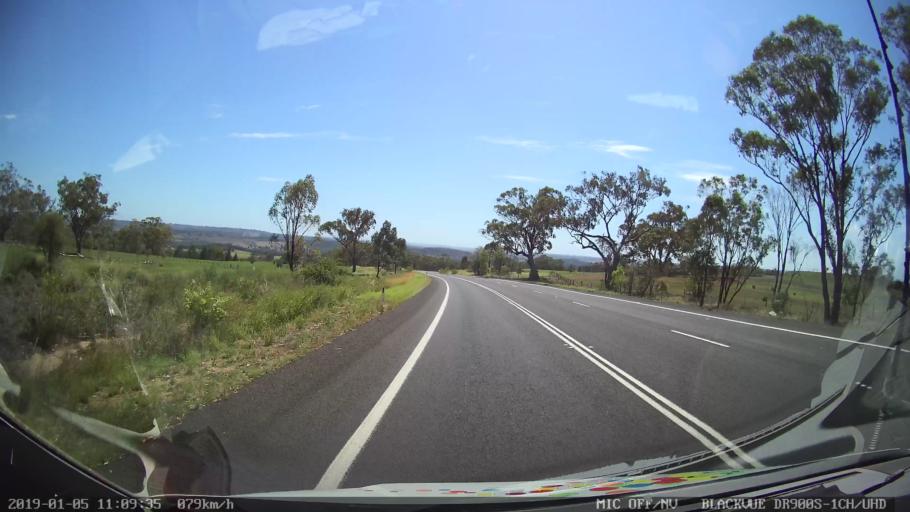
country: AU
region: New South Wales
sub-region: Warrumbungle Shire
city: Coonabarabran
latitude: -31.4127
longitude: 149.2344
